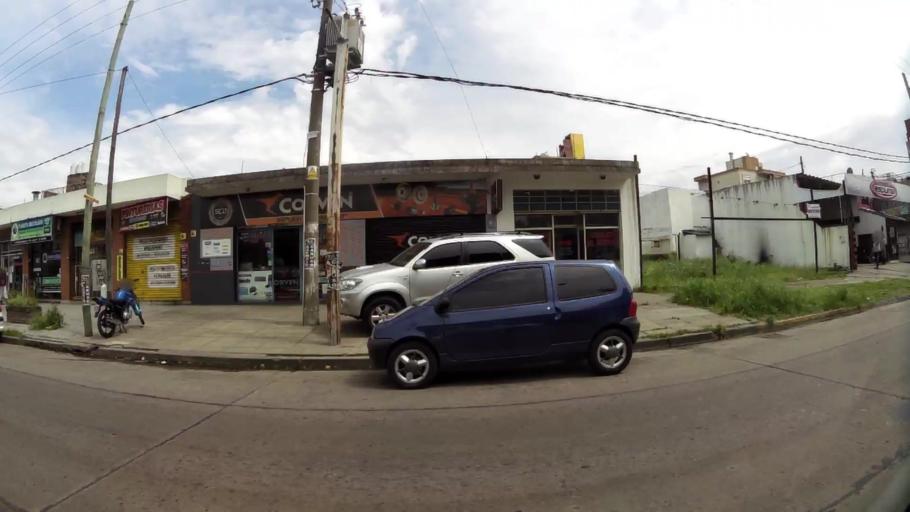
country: AR
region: Buenos Aires F.D.
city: Villa Lugano
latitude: -34.6895
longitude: -58.4974
